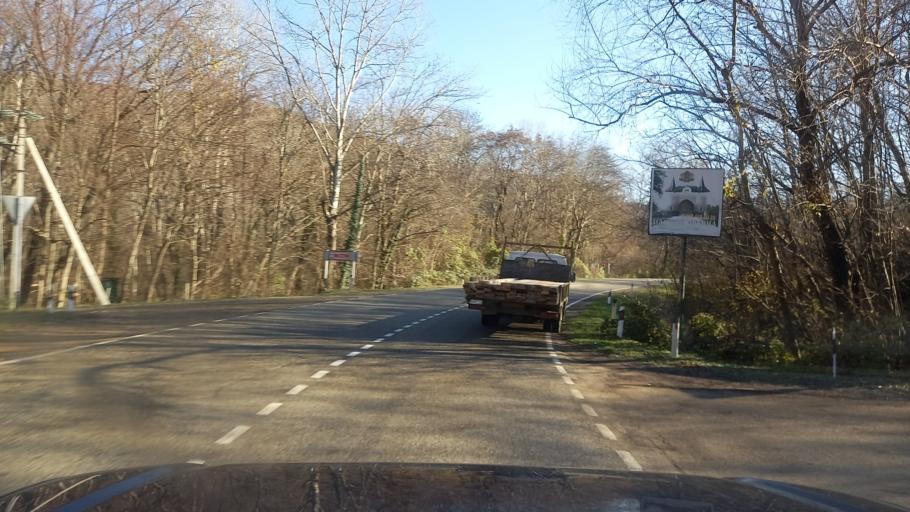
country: RU
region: Krasnodarskiy
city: Goryachiy Klyuch
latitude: 44.6066
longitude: 39.0801
